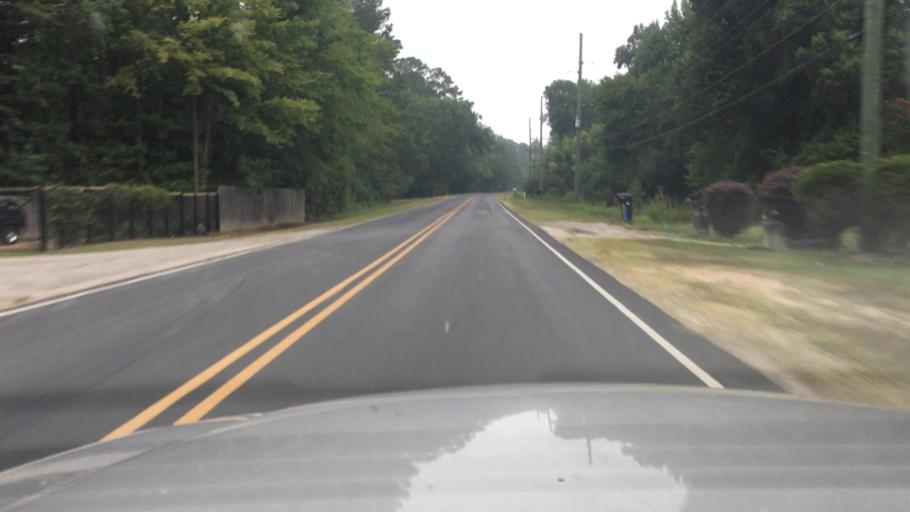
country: US
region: North Carolina
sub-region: Cumberland County
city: Fayetteville
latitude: 34.9993
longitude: -78.8568
